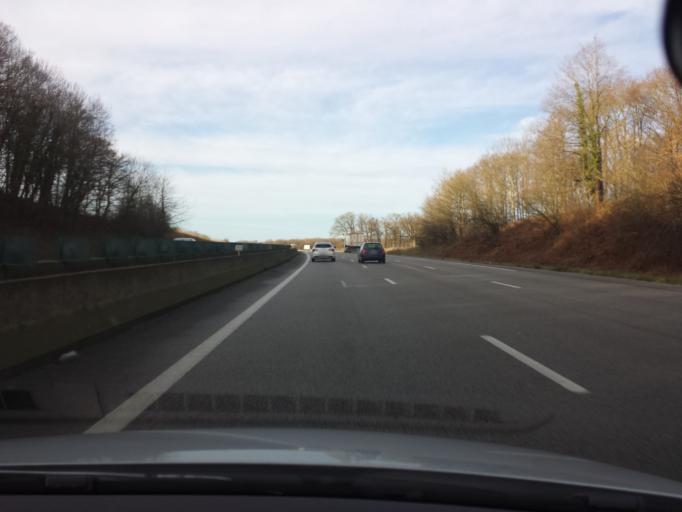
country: FR
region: Ile-de-France
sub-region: Departement des Yvelines
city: Bonnieres-sur-Seine
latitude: 49.0202
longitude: 1.5761
